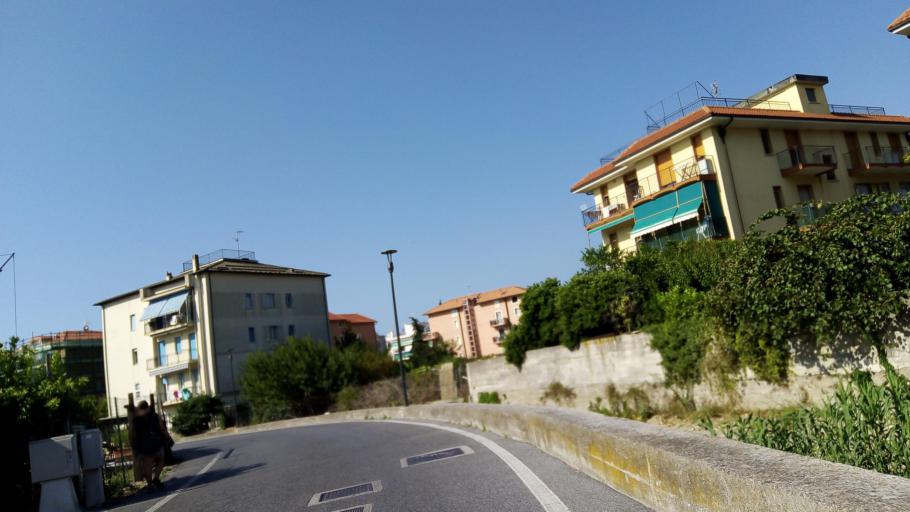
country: IT
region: Liguria
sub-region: Provincia di Savona
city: Borgio
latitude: 44.1584
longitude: 8.3020
